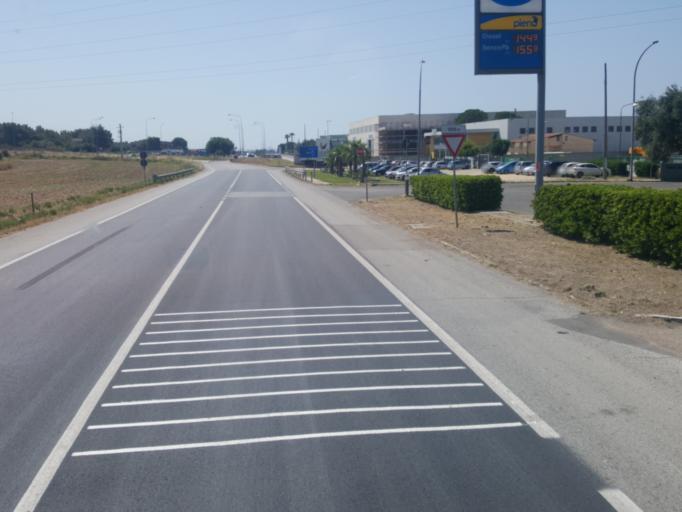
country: IT
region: Apulia
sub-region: Provincia di Taranto
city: Massafra
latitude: 40.5633
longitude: 17.1307
